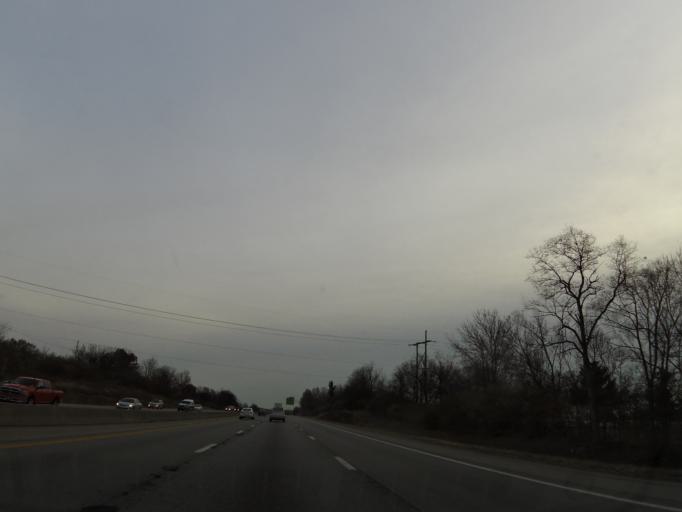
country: US
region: Kentucky
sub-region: Scott County
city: Georgetown
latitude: 38.1310
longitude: -84.5291
